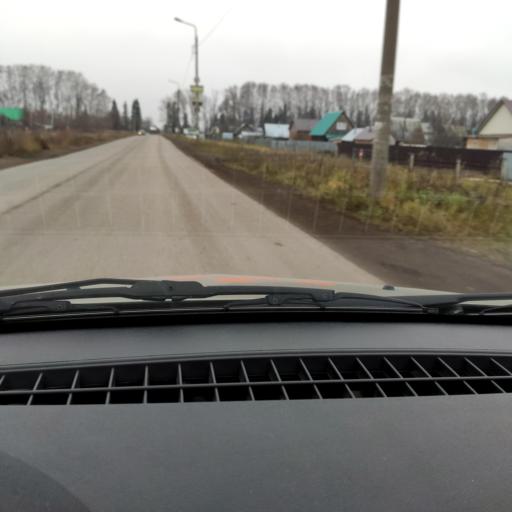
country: RU
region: Bashkortostan
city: Ufa
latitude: 54.5751
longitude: 55.9055
